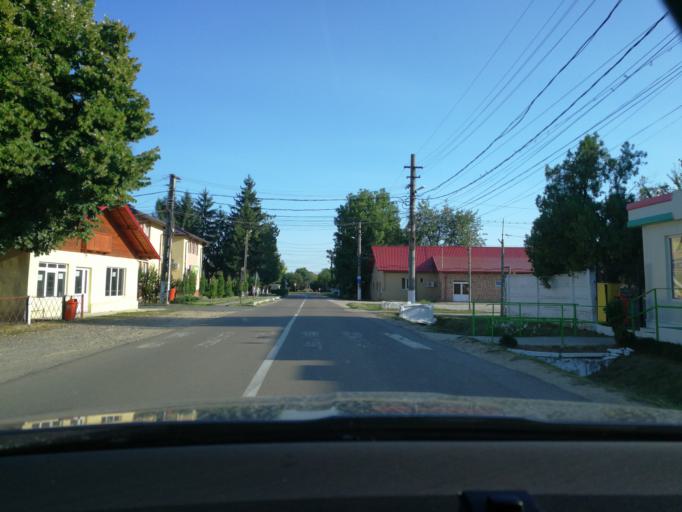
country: RO
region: Prahova
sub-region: Comuna Ceptura
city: Ceptura de Jos
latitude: 45.0206
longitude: 26.3258
